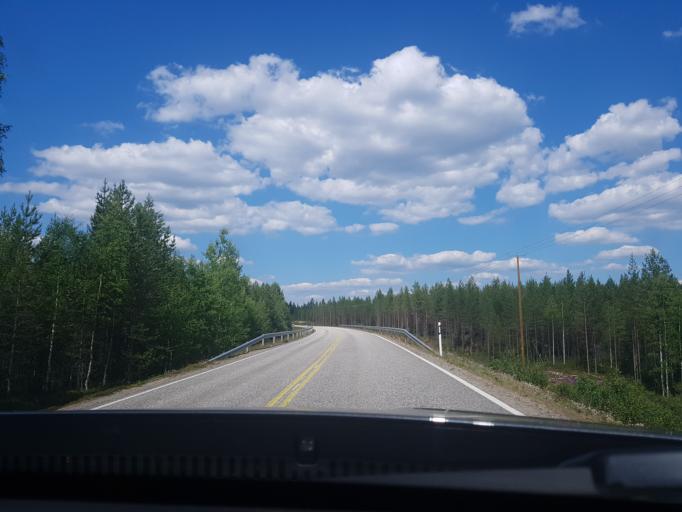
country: FI
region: Kainuu
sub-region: Kehys-Kainuu
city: Kuhmo
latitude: 64.2316
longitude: 29.8191
